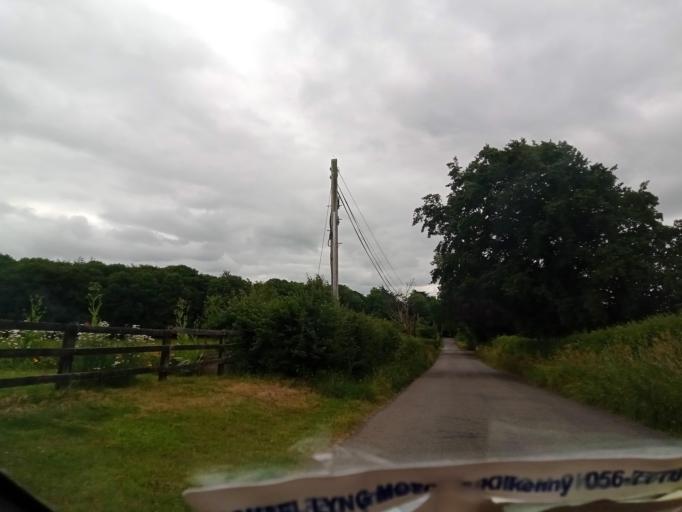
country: IE
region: Leinster
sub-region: Kilkenny
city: Ballyragget
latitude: 52.7441
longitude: -7.4193
